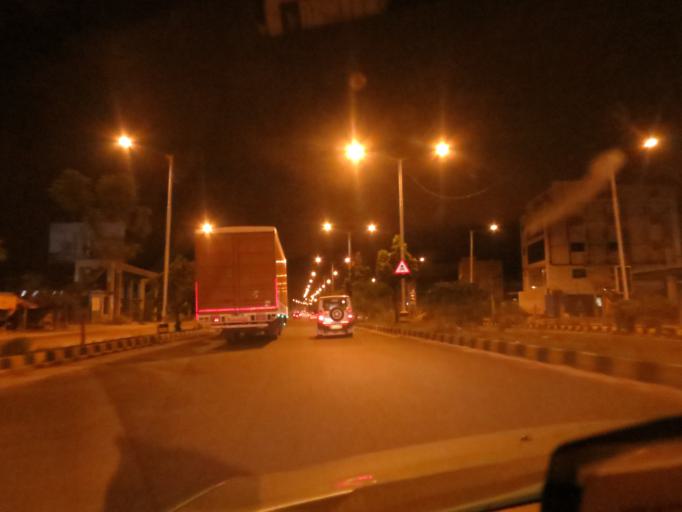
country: IN
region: Karnataka
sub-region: Bangalore Urban
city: Bangalore
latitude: 12.9939
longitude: 77.6854
